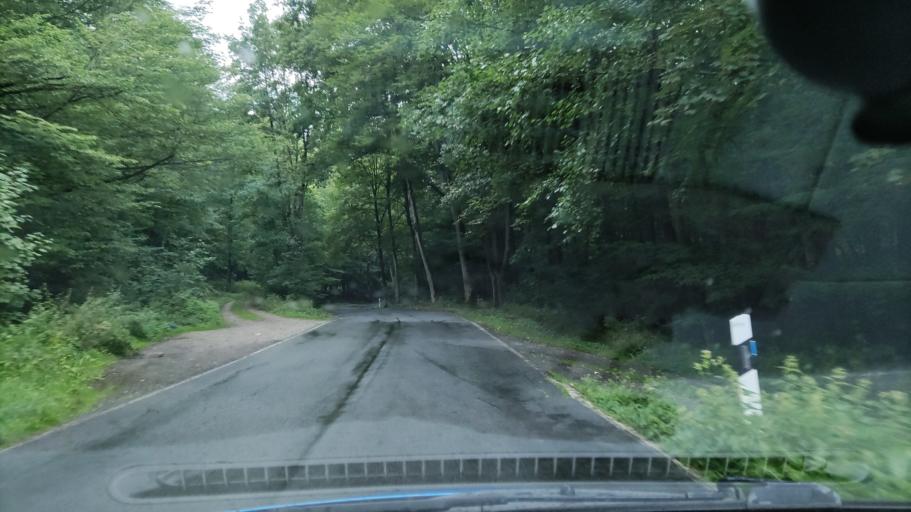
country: DE
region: Lower Saxony
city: Coppengrave
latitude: 51.9623
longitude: 9.7662
